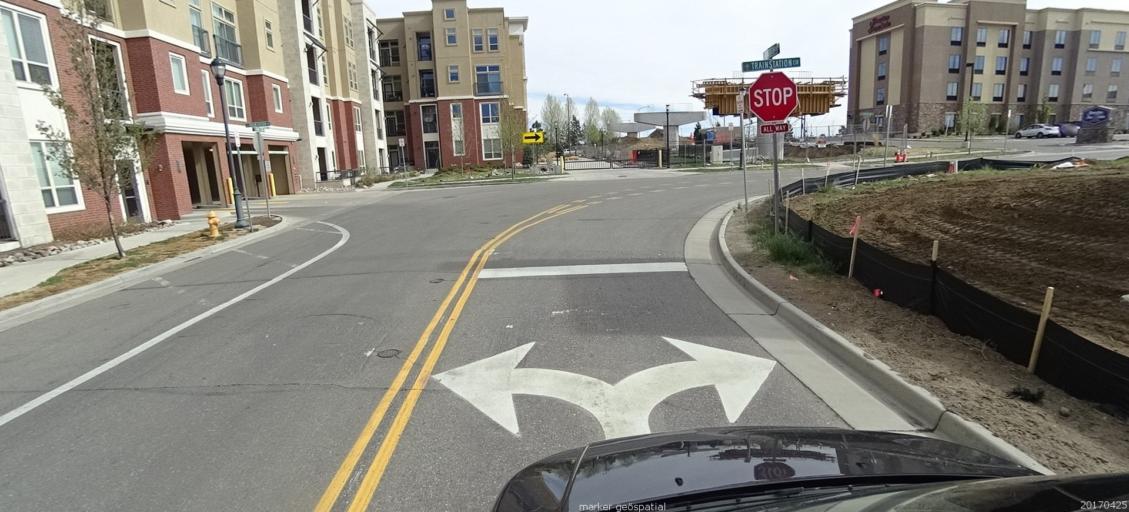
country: US
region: Colorado
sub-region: Douglas County
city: Meridian
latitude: 39.5351
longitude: -104.8713
